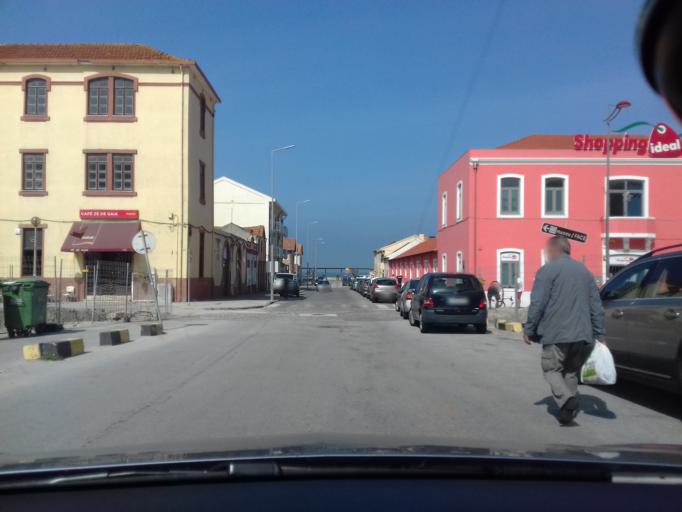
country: PT
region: Aveiro
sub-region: Espinho
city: Espinho
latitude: 41.0040
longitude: -8.6442
